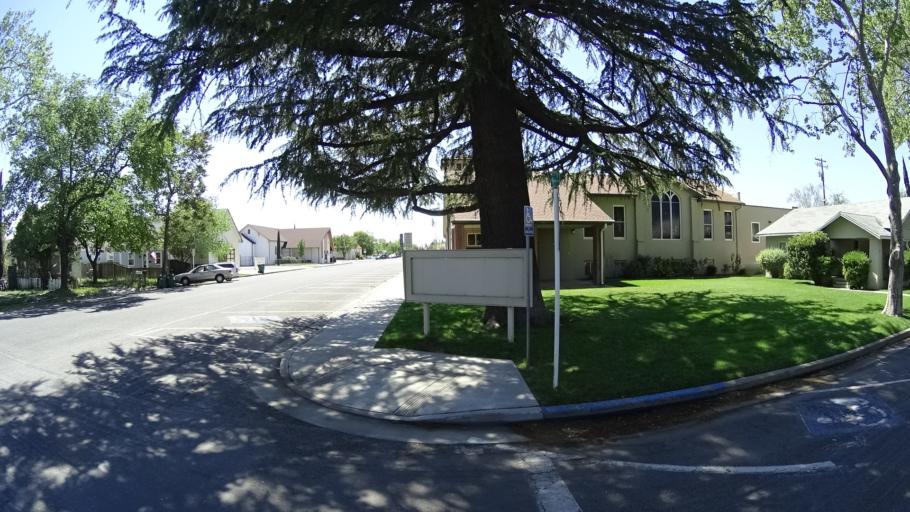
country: US
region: California
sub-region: Glenn County
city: Orland
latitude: 39.7485
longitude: -122.1891
